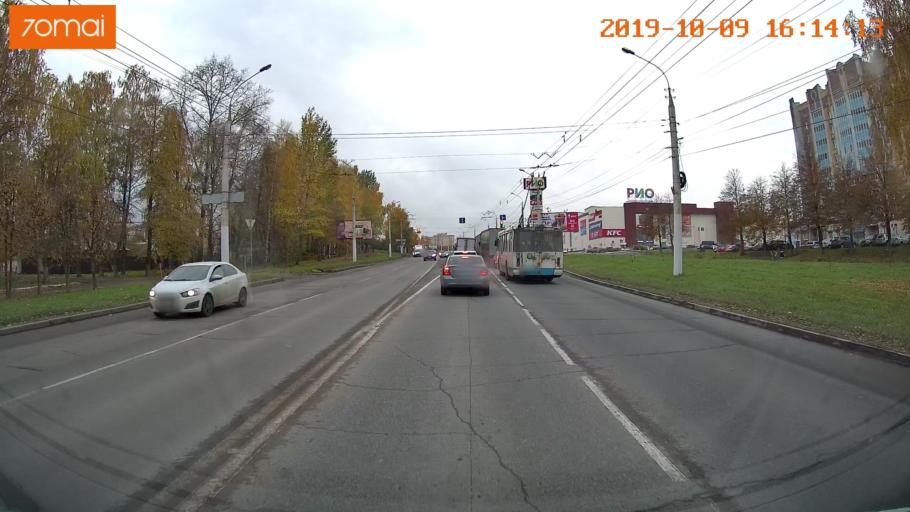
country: RU
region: Kostroma
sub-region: Kostromskoy Rayon
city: Kostroma
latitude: 57.7431
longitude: 40.9225
